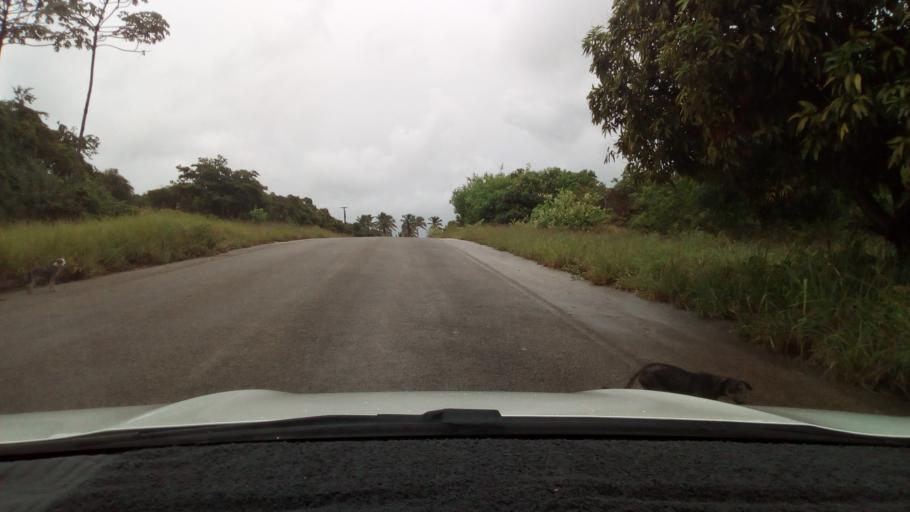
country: BR
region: Paraiba
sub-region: Pitimbu
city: Pitimbu
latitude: -7.4495
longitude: -34.8362
